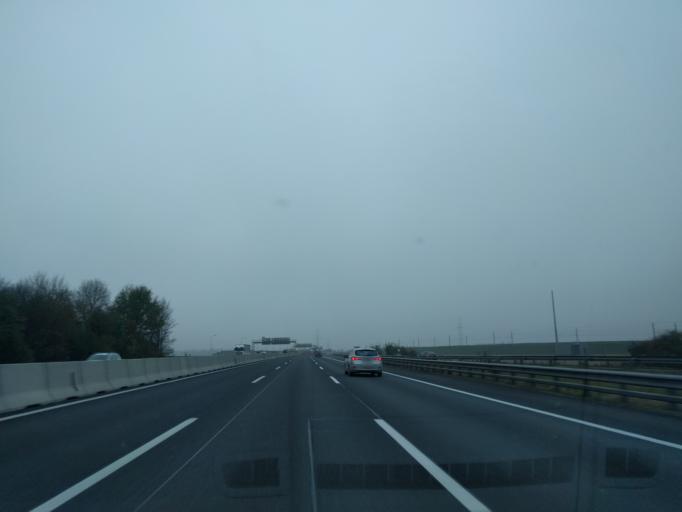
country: AT
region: Lower Austria
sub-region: Sankt Polten Stadt
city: Sankt Poelten
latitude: 48.1788
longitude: 15.6589
